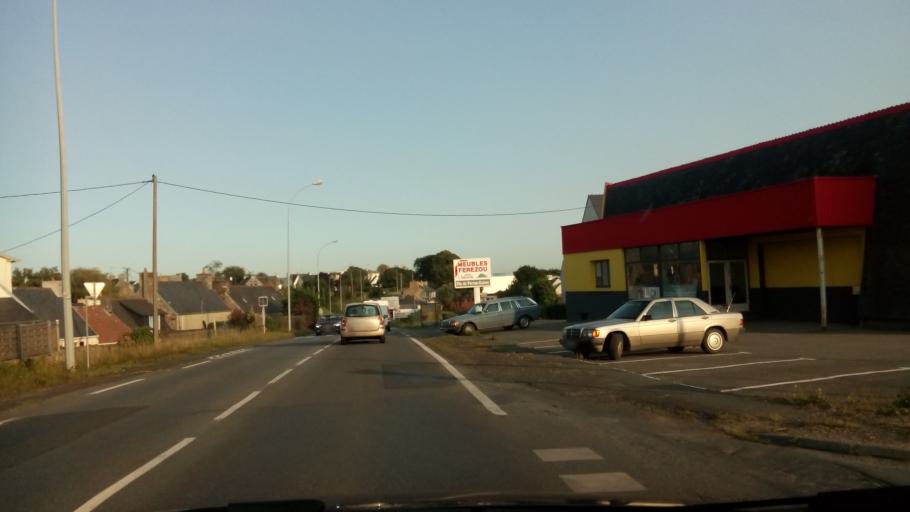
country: FR
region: Brittany
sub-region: Departement des Cotes-d'Armor
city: Lannion
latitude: 48.7465
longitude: -3.4800
